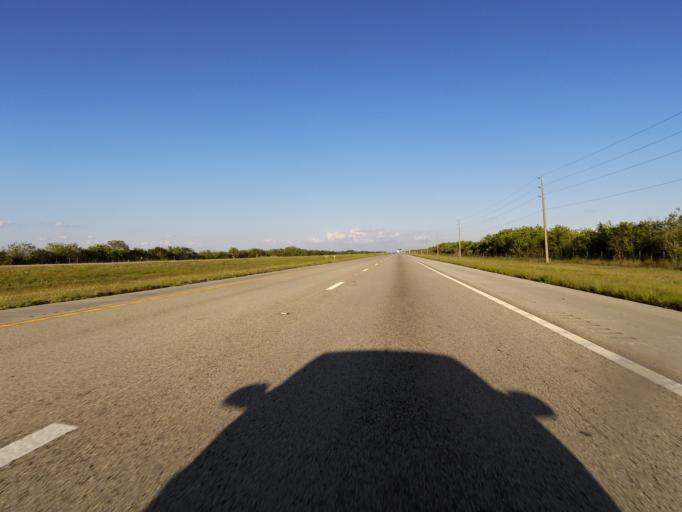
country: US
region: Florida
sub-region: Broward County
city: Weston
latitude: 26.1630
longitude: -80.8074
